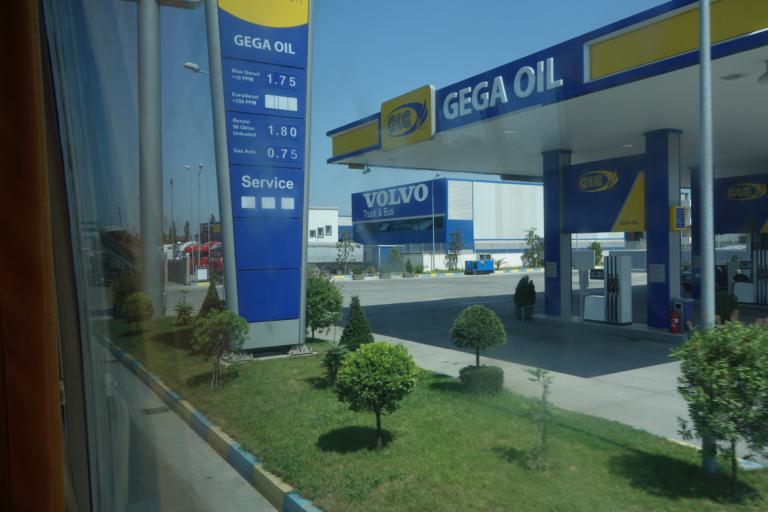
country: AL
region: Durres
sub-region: Rrethi i Durresit
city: Rrashbull
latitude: 41.3389
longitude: 19.4884
